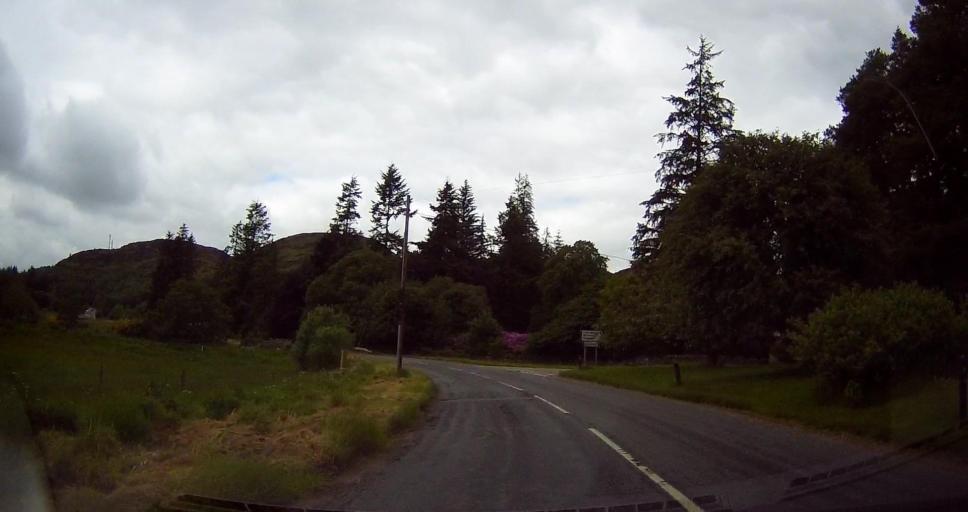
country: GB
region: Scotland
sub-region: Highland
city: Dornoch
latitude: 58.0047
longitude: -4.1769
